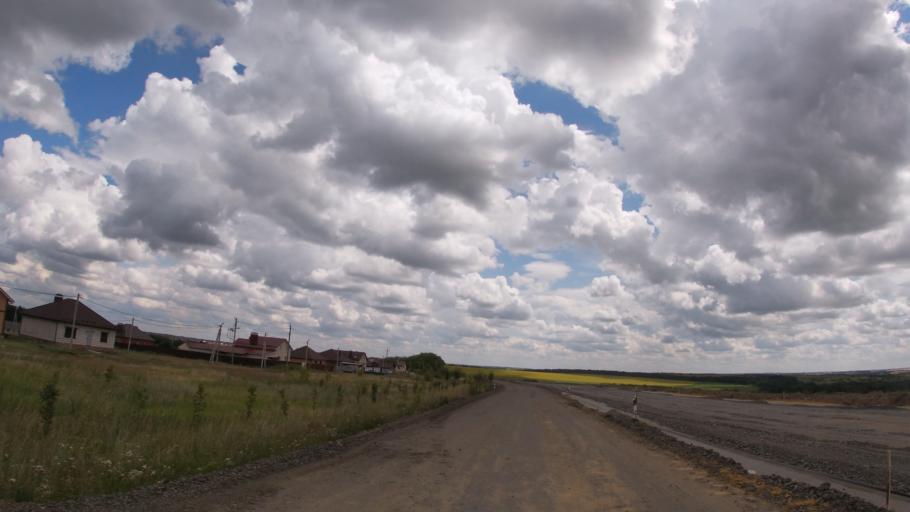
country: RU
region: Belgorod
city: Mayskiy
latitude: 50.5015
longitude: 36.4476
